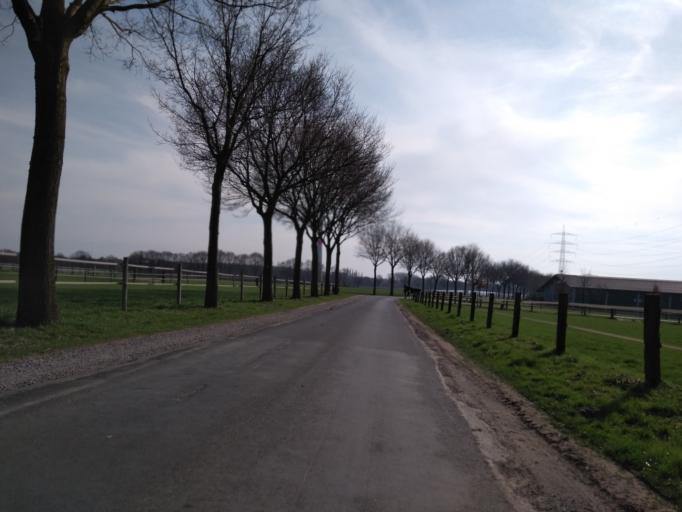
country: DE
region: North Rhine-Westphalia
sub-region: Regierungsbezirk Munster
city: Gladbeck
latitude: 51.5952
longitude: 6.9452
